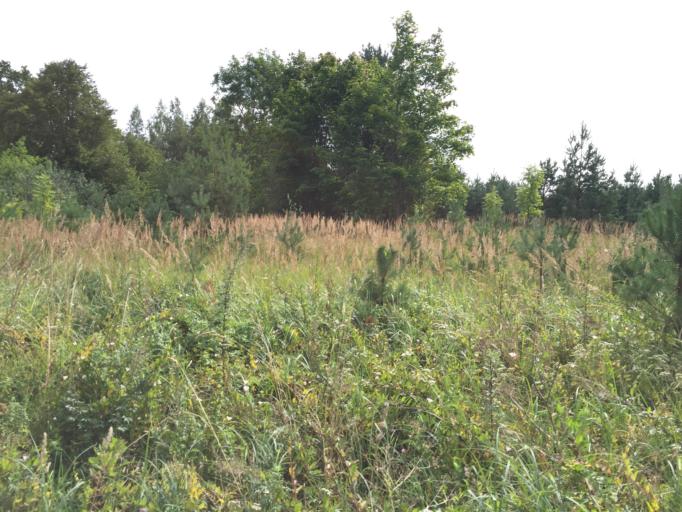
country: LV
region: Cibla
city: Cibla
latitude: 56.2412
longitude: 27.8302
